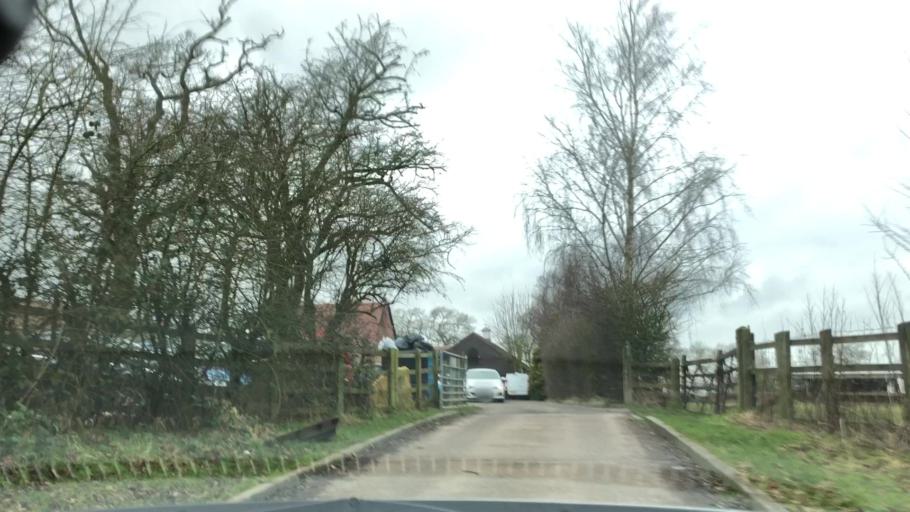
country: GB
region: England
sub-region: Coventry
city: Keresley
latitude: 52.4364
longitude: -1.5514
